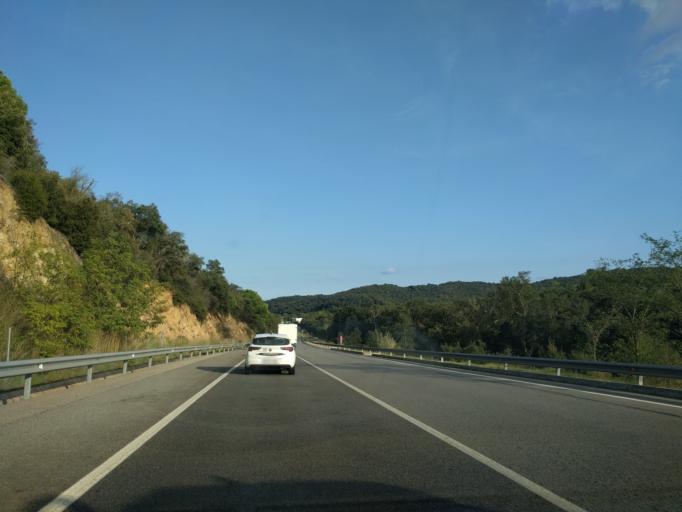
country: ES
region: Catalonia
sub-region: Provincia de Girona
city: Llagostera
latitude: 41.8289
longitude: 2.9375
